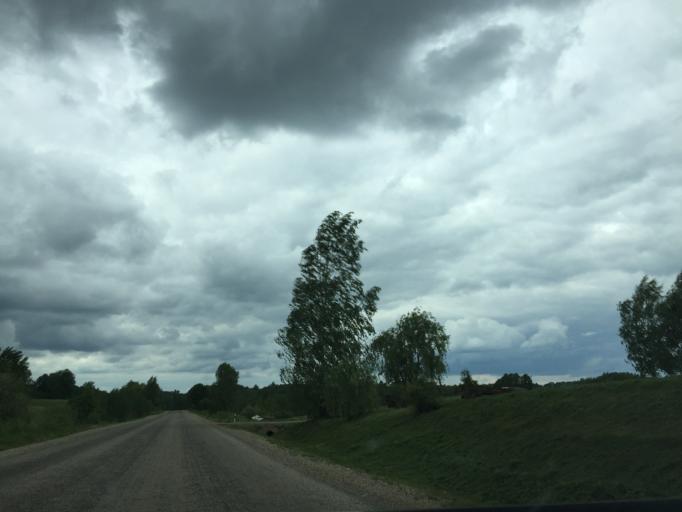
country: LV
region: Dagda
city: Dagda
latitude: 56.0778
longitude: 27.5401
